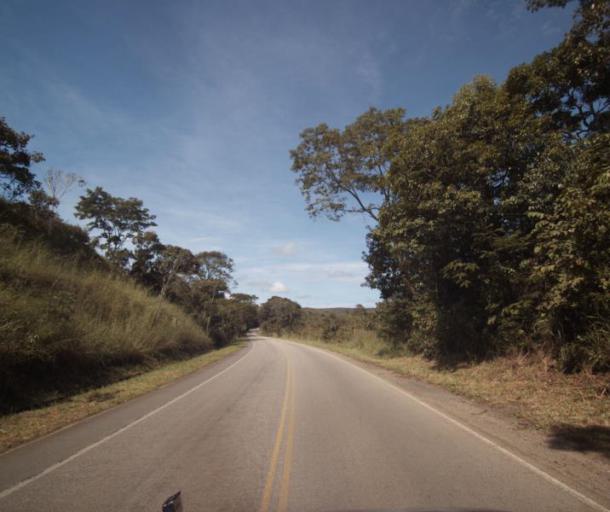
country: BR
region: Goias
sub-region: Abadiania
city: Abadiania
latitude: -16.1208
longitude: -48.8944
